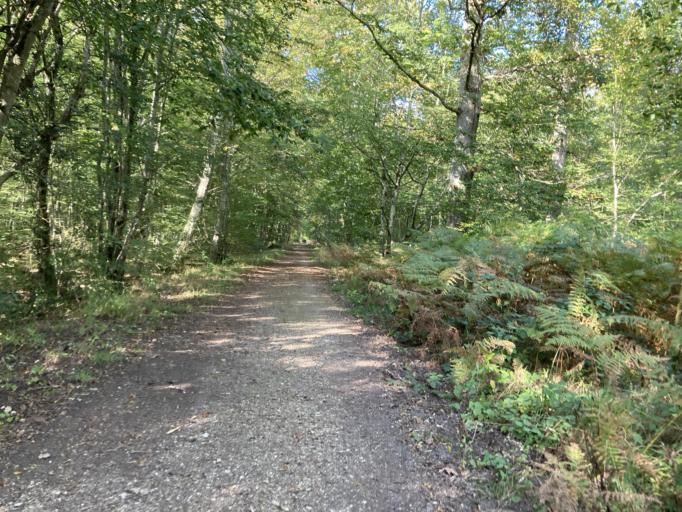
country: FR
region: Ile-de-France
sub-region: Departement de Seine-et-Marne
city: La Rochette
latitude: 48.4739
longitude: 2.6566
